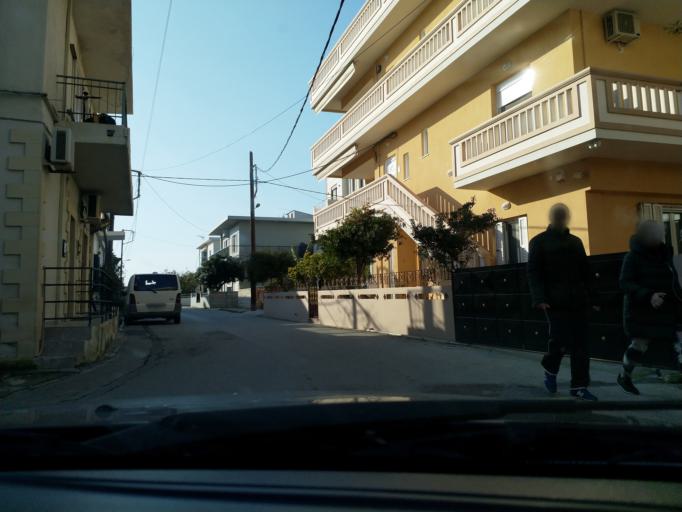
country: GR
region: Crete
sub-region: Nomos Chanias
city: Chania
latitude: 35.5009
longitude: 24.0242
